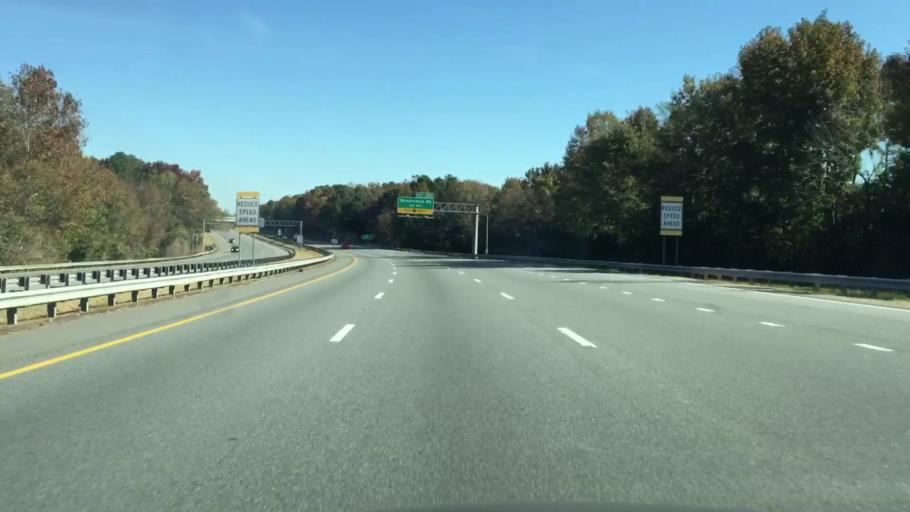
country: US
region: North Carolina
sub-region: Guilford County
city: Greensboro
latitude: 36.0246
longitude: -79.8135
